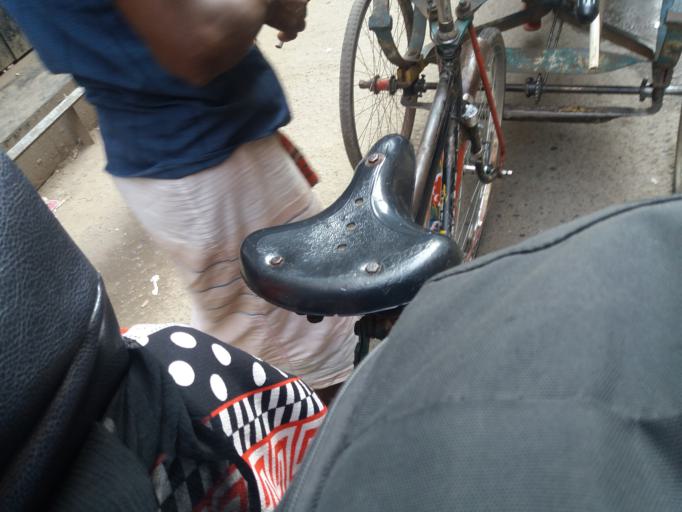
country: BD
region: Dhaka
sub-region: Dhaka
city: Dhaka
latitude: 23.7227
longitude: 90.3999
